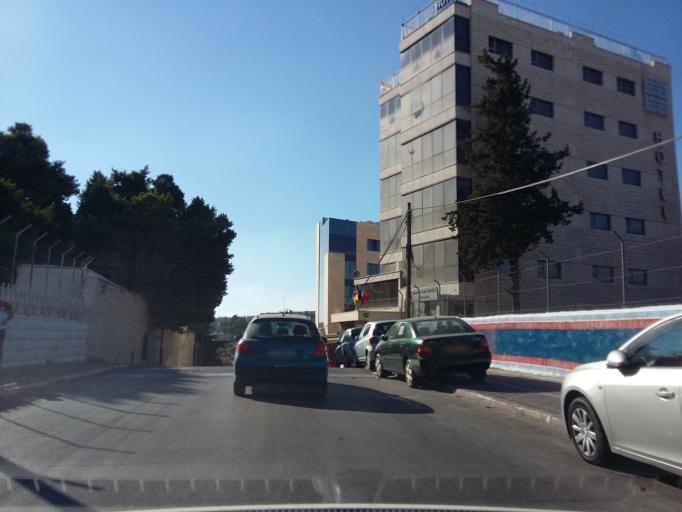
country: PS
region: West Bank
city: East Jerusalem
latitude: 31.7900
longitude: 35.2313
